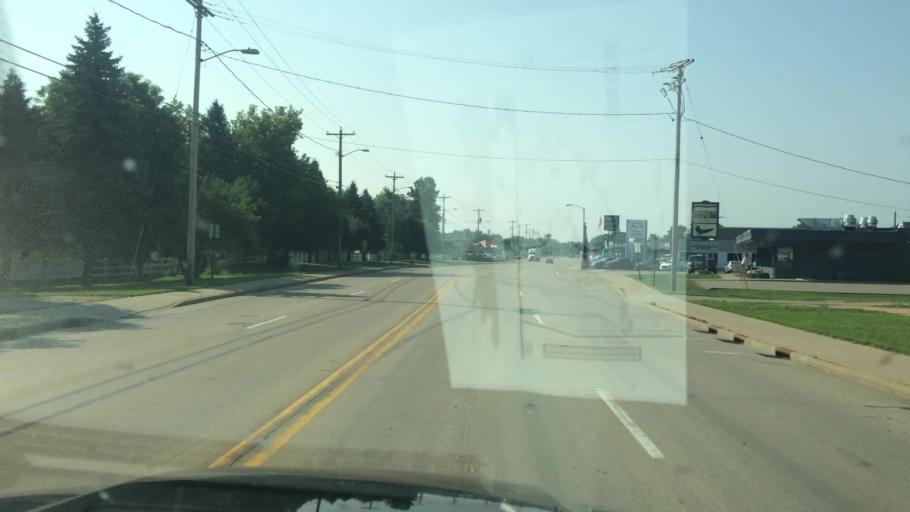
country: US
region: Wisconsin
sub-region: Marathon County
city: Schofield
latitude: 44.9289
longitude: -89.6142
